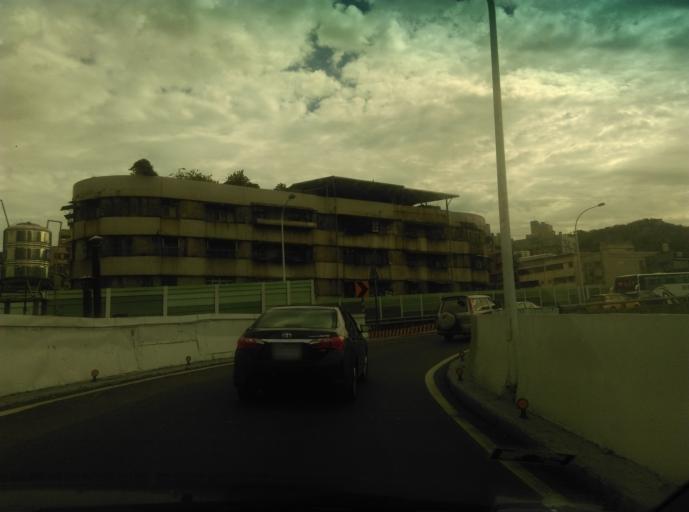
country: TW
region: Taiwan
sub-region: Keelung
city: Keelung
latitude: 25.1281
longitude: 121.7387
